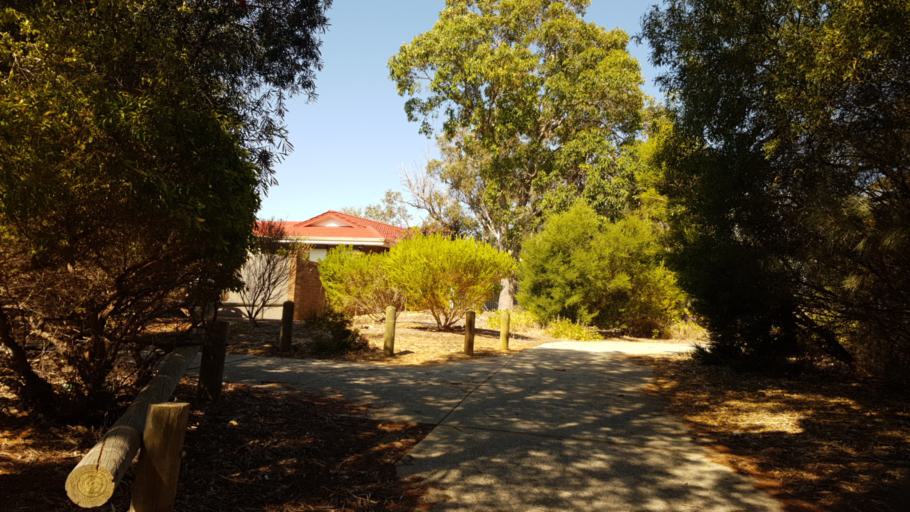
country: AU
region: Western Australia
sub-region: Stirling
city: Karrinyup
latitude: -31.8566
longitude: 115.7765
